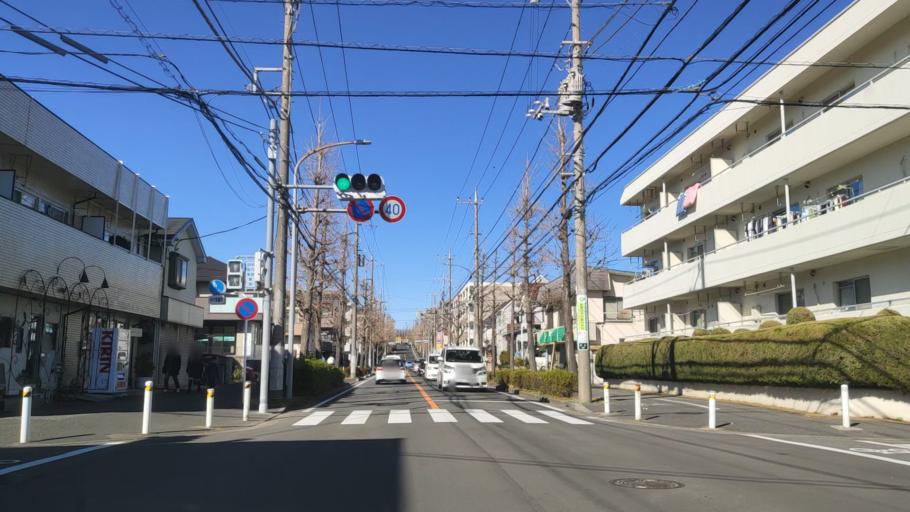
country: JP
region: Tokyo
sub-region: Machida-shi
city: Machida
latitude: 35.5491
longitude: 139.5084
